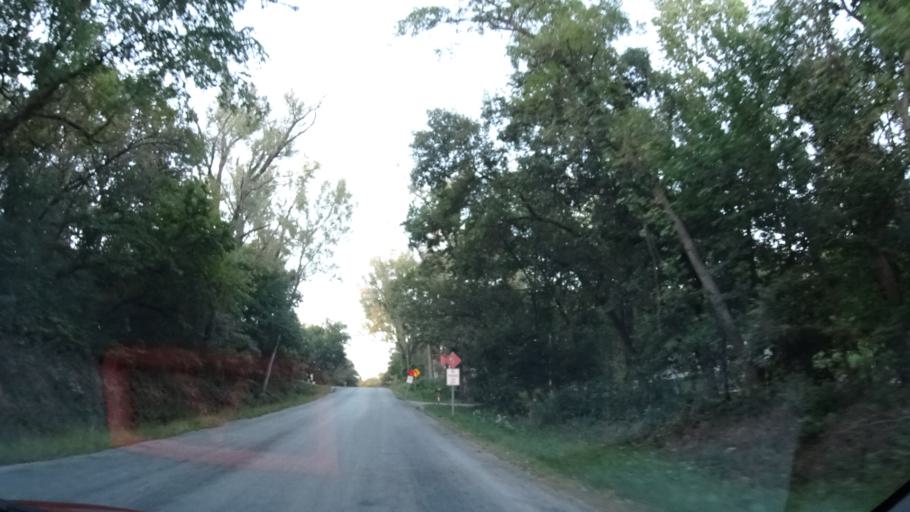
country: US
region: Iowa
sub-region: Pottawattamie County
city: Council Bluffs
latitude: 41.3028
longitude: -95.8559
